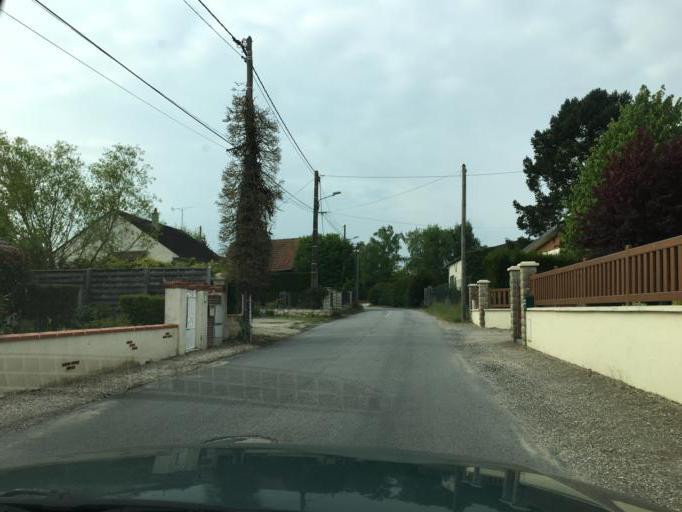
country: FR
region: Centre
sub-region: Departement du Loiret
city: Clery-Saint-Andre
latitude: 47.8185
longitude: 1.7651
